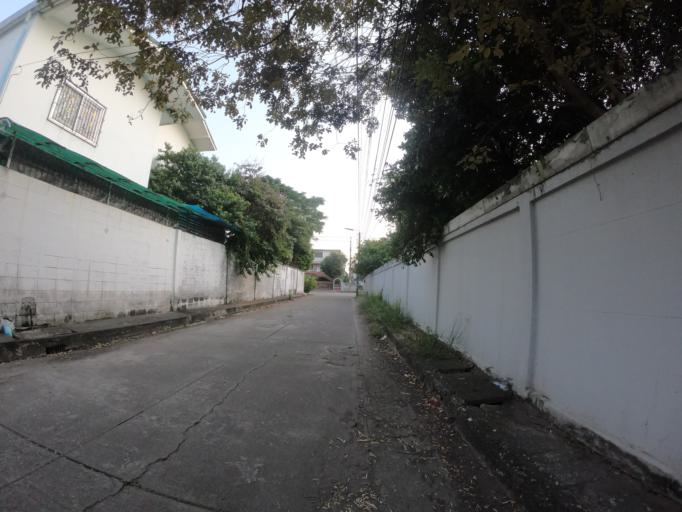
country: TH
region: Bangkok
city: Lat Phrao
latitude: 13.8256
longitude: 100.6076
